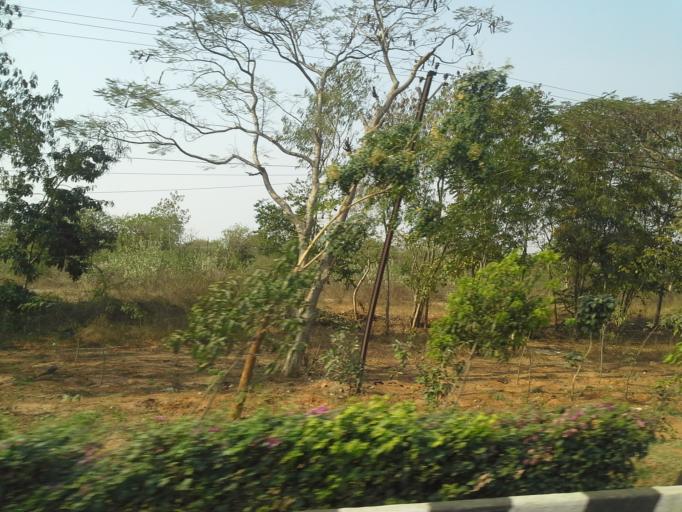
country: IN
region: Telangana
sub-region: Rangareddi
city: Balapur
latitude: 17.2754
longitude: 78.4020
